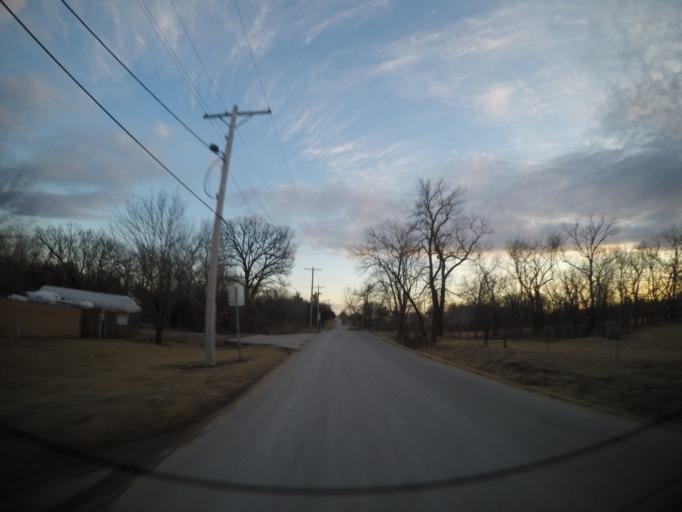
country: US
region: Kansas
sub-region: Wyandotte County
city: Bonner Springs
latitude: 39.0514
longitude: -94.9088
